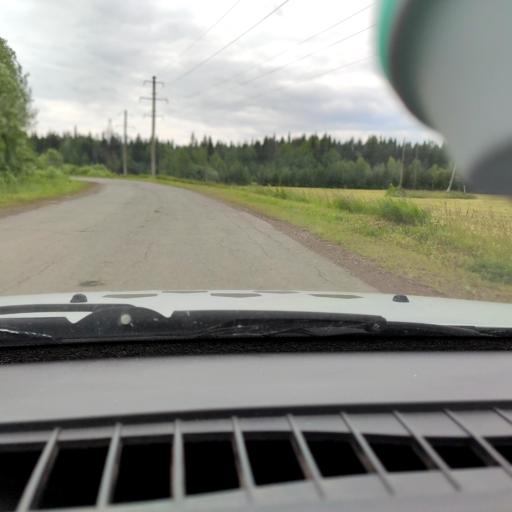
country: RU
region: Perm
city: Uinskoye
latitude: 57.1279
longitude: 56.5581
